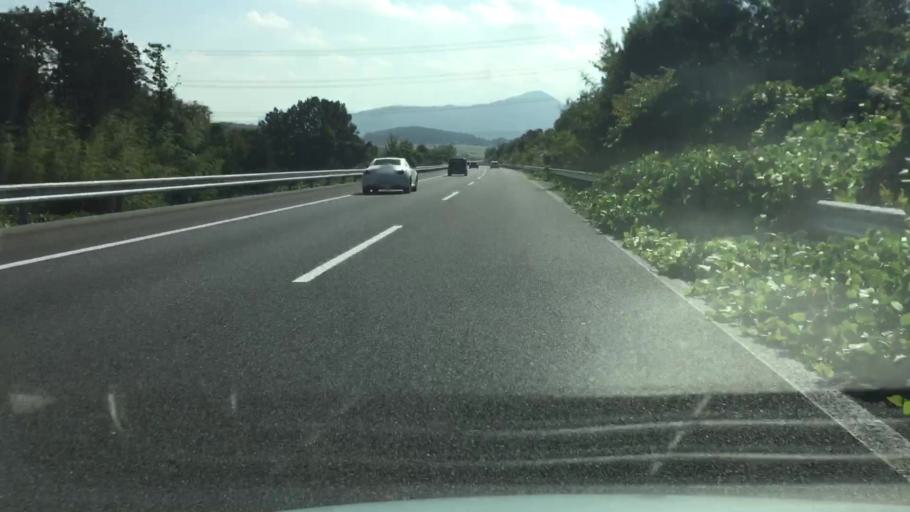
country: JP
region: Ibaraki
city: Iwase
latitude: 36.3690
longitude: 140.0506
